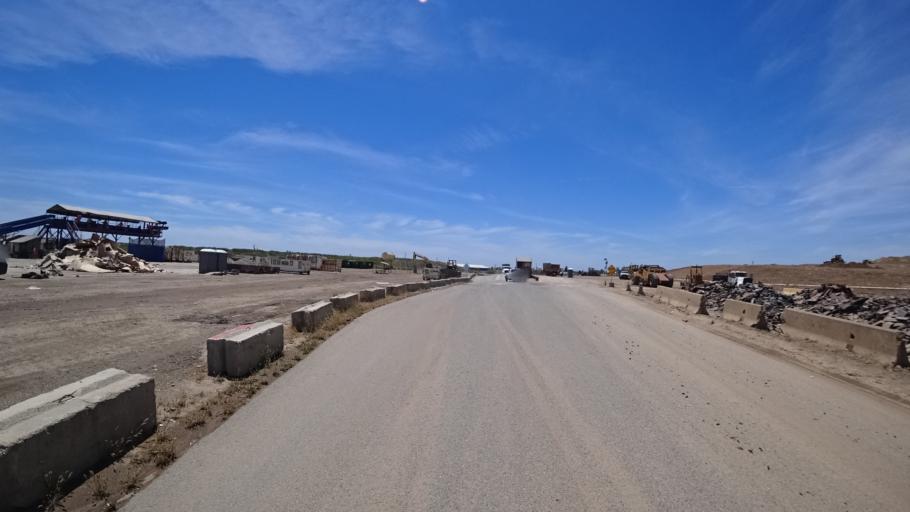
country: US
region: California
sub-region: Sacramento County
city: Rosemont
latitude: 38.5269
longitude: -121.3825
